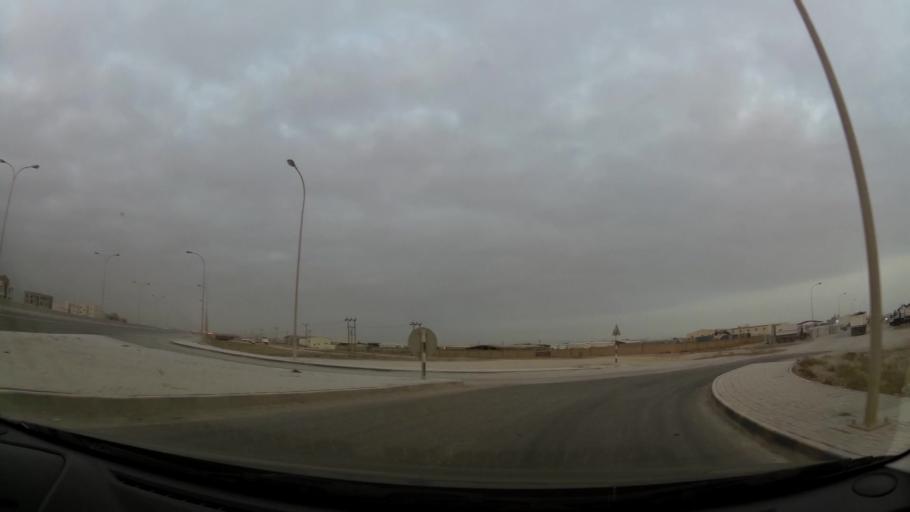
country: OM
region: Zufar
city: Salalah
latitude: 17.0374
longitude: 54.0416
